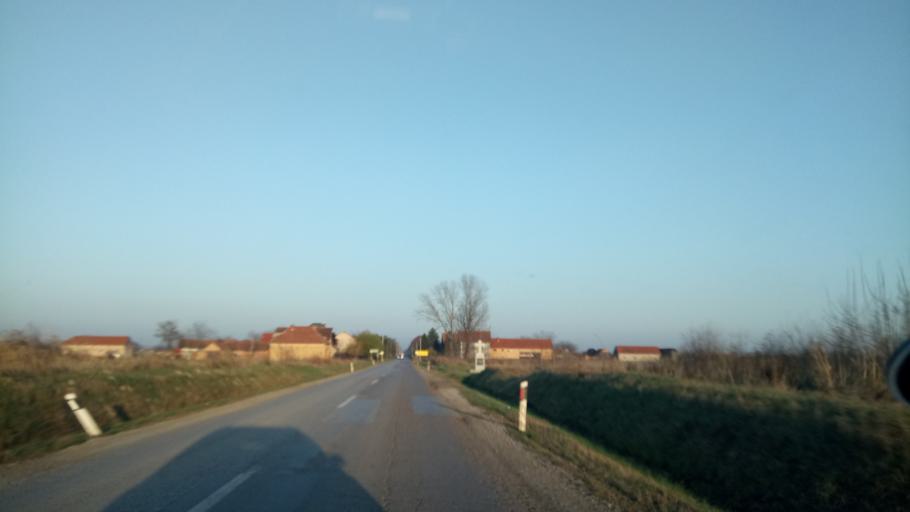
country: RS
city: Novi Karlovci
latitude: 45.0748
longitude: 20.1585
